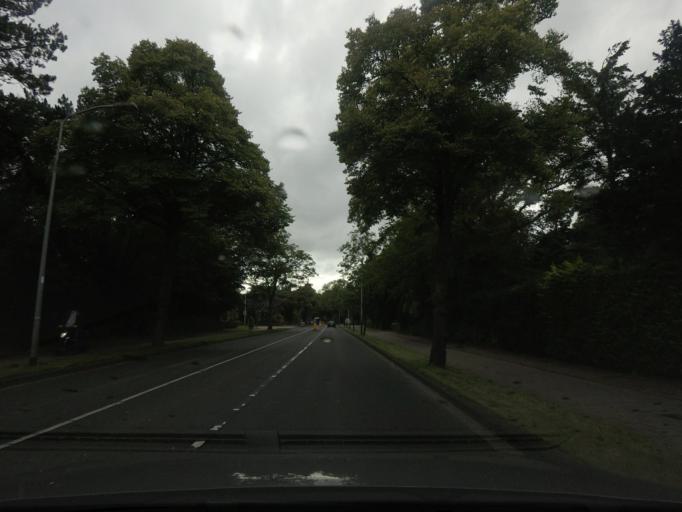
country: NL
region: North Holland
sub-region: Gemeente Heemstede
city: Heemstede
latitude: 52.3642
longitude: 4.5827
